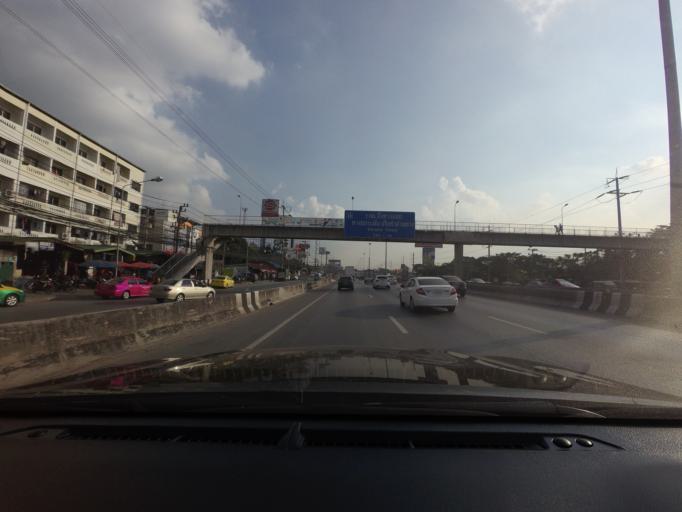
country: TH
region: Pathum Thani
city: Khlong Luang
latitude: 14.0194
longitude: 100.6157
